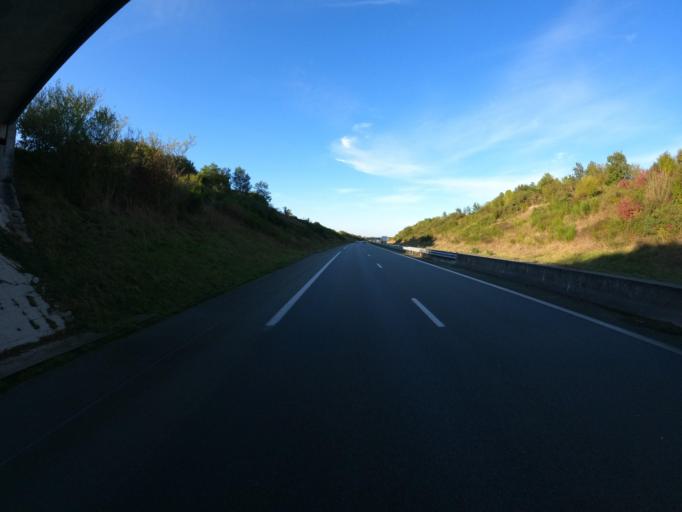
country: FR
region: Pays de la Loire
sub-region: Departement de Maine-et-Loire
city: Nuaille
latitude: 47.1076
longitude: -0.8274
